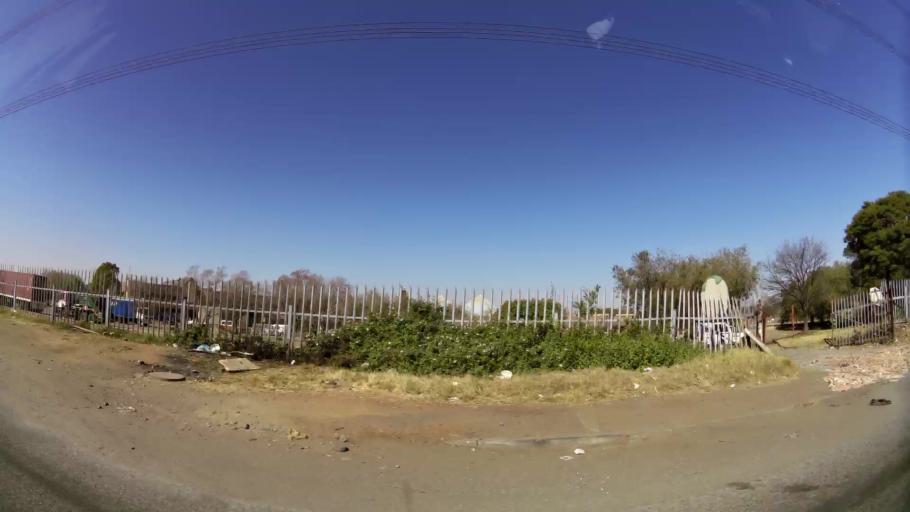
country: ZA
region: Gauteng
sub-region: City of Johannesburg Metropolitan Municipality
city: Modderfontein
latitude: -26.0813
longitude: 28.1871
